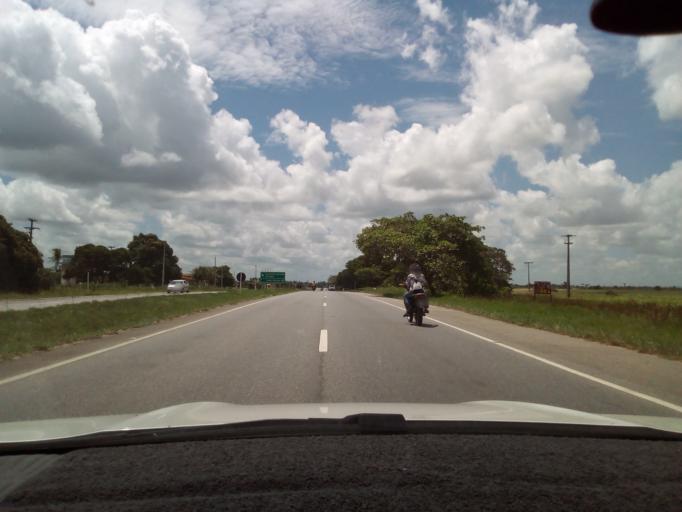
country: BR
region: Paraiba
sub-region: Pilar
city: Pilar
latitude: -7.1868
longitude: -35.2882
